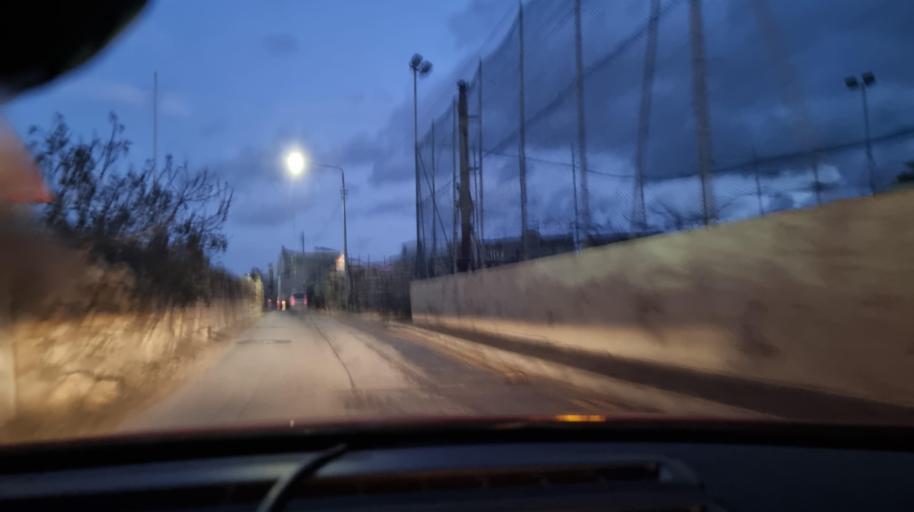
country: MT
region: Qormi
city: Qormi
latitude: 35.8824
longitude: 14.4757
